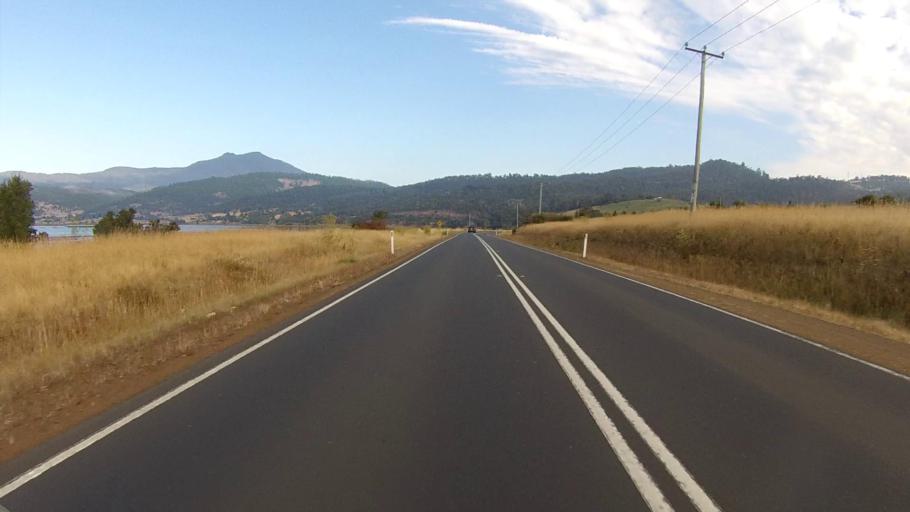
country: AU
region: Tasmania
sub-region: Brighton
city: Bridgewater
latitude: -42.7303
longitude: 147.2092
